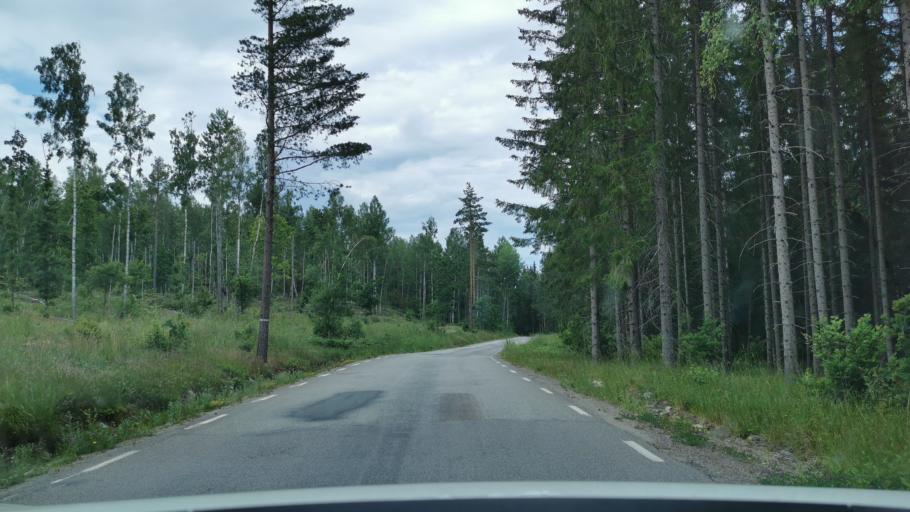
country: SE
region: Vaestra Goetaland
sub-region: Bengtsfors Kommun
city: Dals Langed
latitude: 58.8503
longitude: 12.4059
